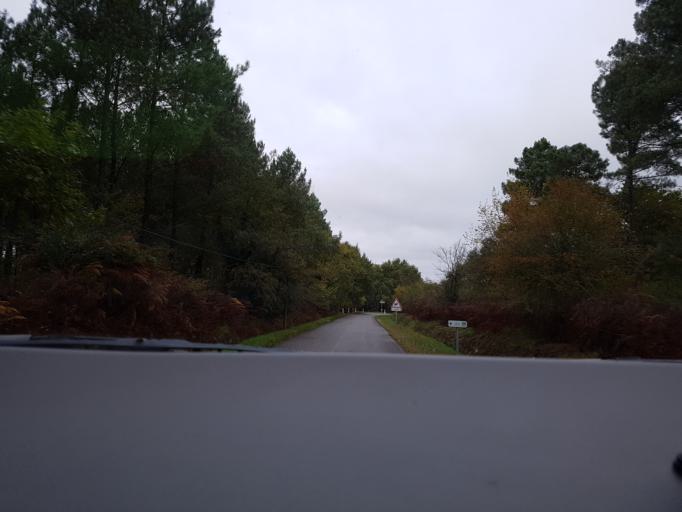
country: FR
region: Aquitaine
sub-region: Departement des Landes
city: Roquefort
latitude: 44.0572
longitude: -0.3493
